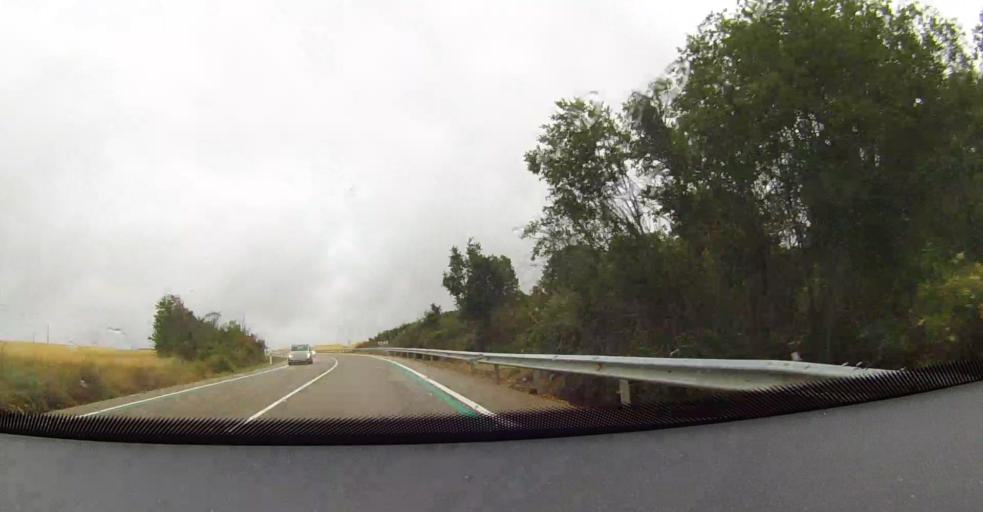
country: ES
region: Castille and Leon
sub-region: Provincia de Palencia
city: Villaluenga de la Vega
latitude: 42.5628
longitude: -4.7527
